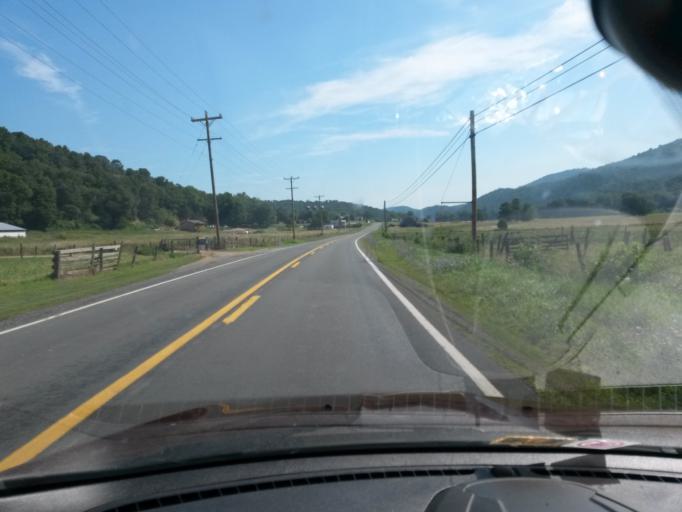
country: US
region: Virginia
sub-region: Shenandoah County
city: Basye
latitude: 38.9725
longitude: -78.7983
